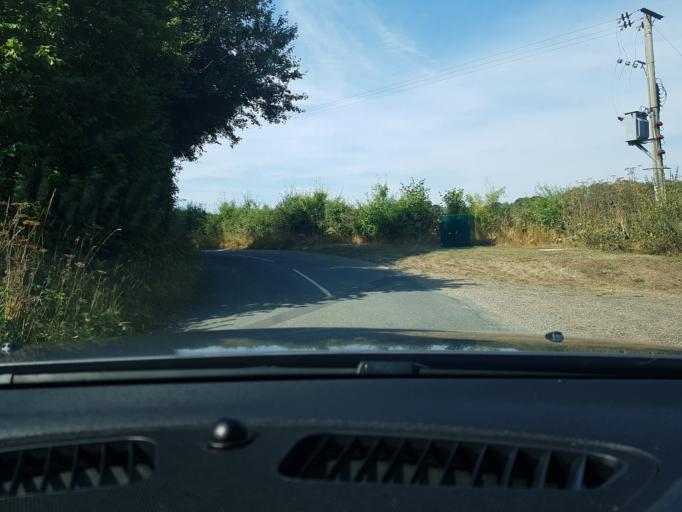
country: GB
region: England
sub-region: West Berkshire
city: Hungerford
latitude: 51.4416
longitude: -1.5050
